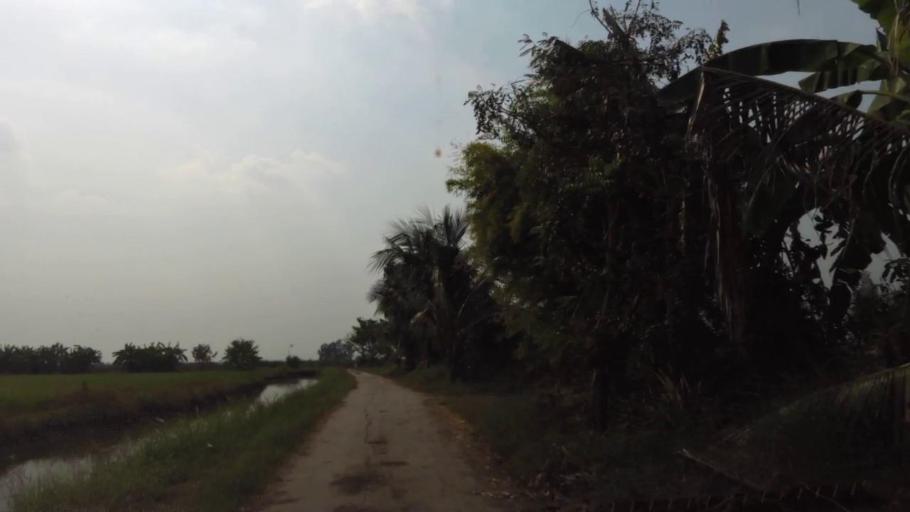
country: TH
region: Phra Nakhon Si Ayutthaya
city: Phra Nakhon Si Ayutthaya
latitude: 14.3143
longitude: 100.5568
